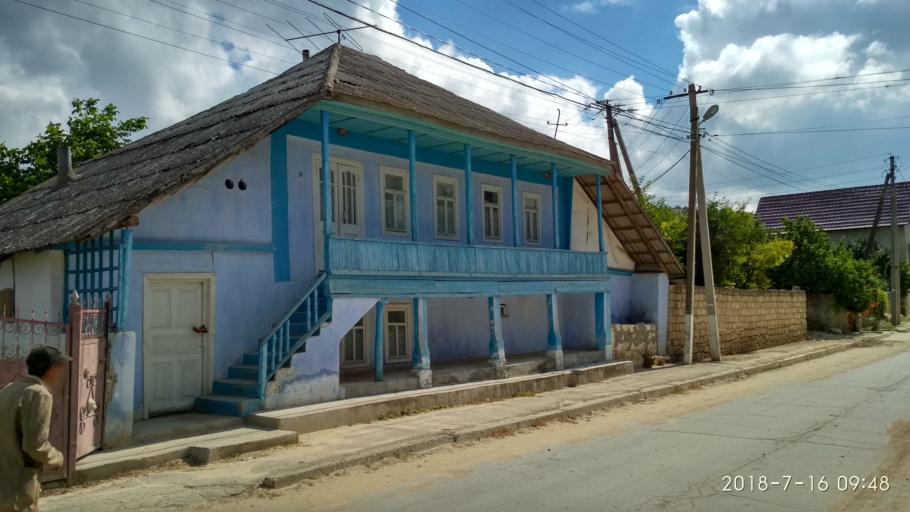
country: MD
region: Telenesti
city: Cocieri
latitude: 47.3111
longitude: 28.9763
